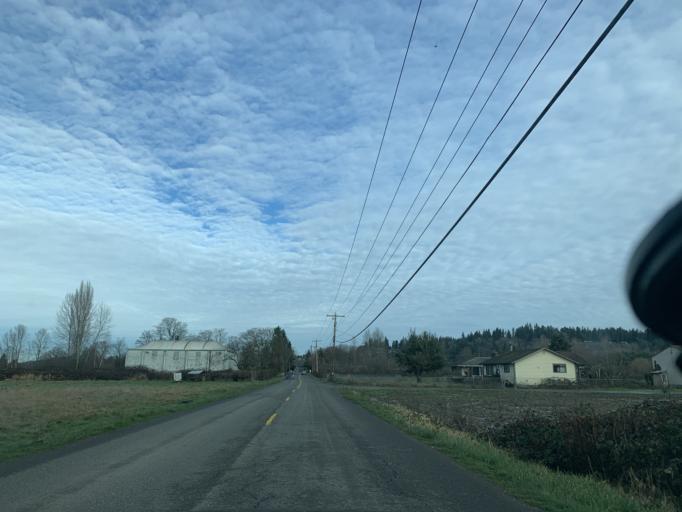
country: US
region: Washington
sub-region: Pierce County
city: Milton
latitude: 47.2163
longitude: -122.3205
